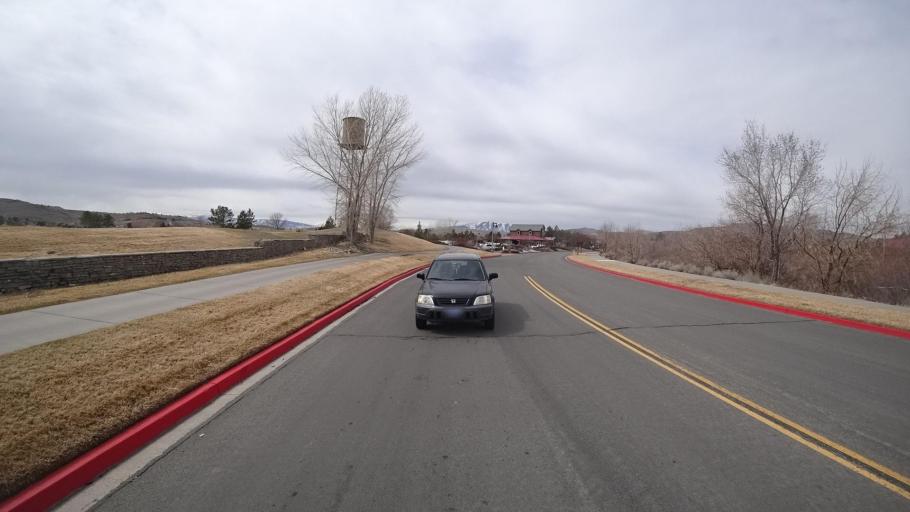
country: US
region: Nevada
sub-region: Washoe County
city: Spanish Springs
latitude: 39.6109
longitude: -119.6875
